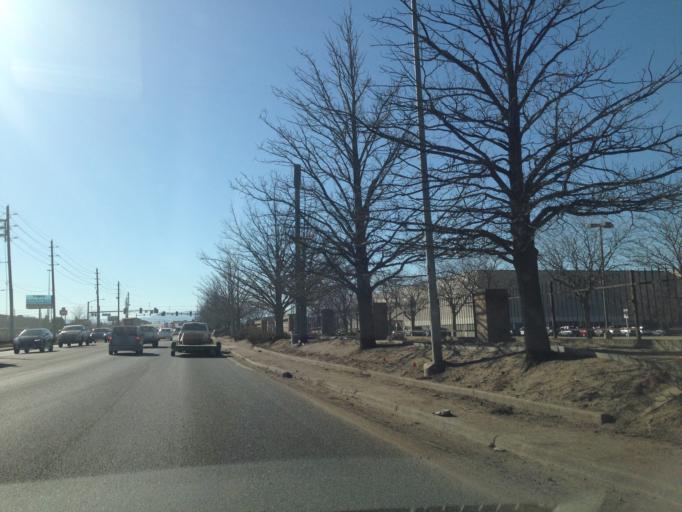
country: US
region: Colorado
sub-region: Adams County
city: Twin Lakes
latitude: 39.8020
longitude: -104.9790
